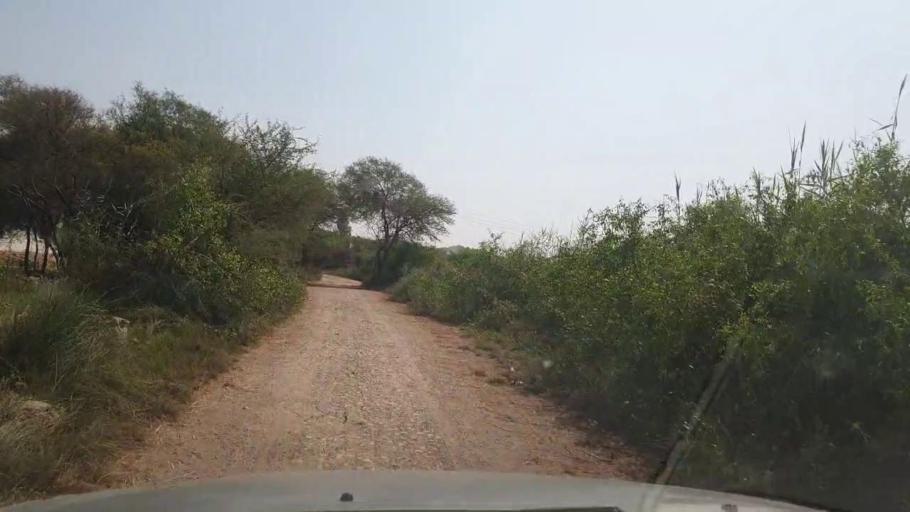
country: PK
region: Sindh
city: Bulri
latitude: 24.8826
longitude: 68.4026
